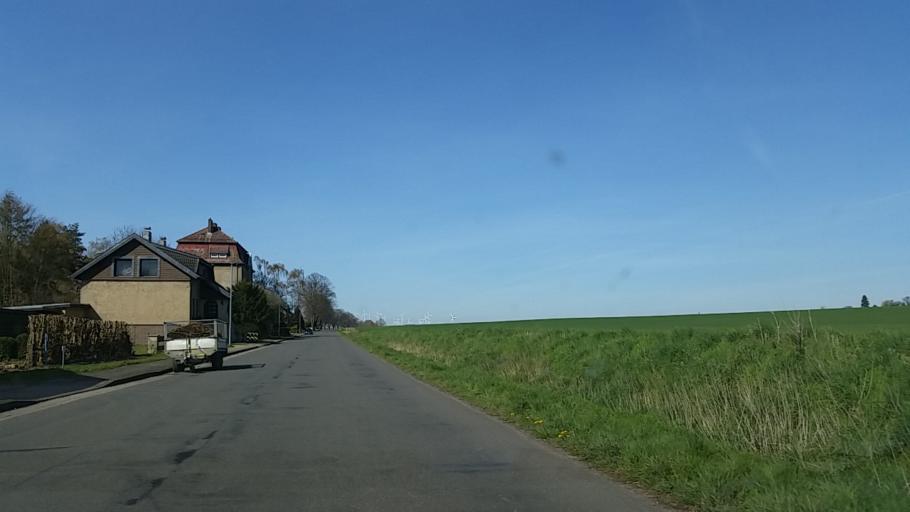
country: DE
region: Lower Saxony
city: Beierstedt
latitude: 52.0672
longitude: 10.8771
